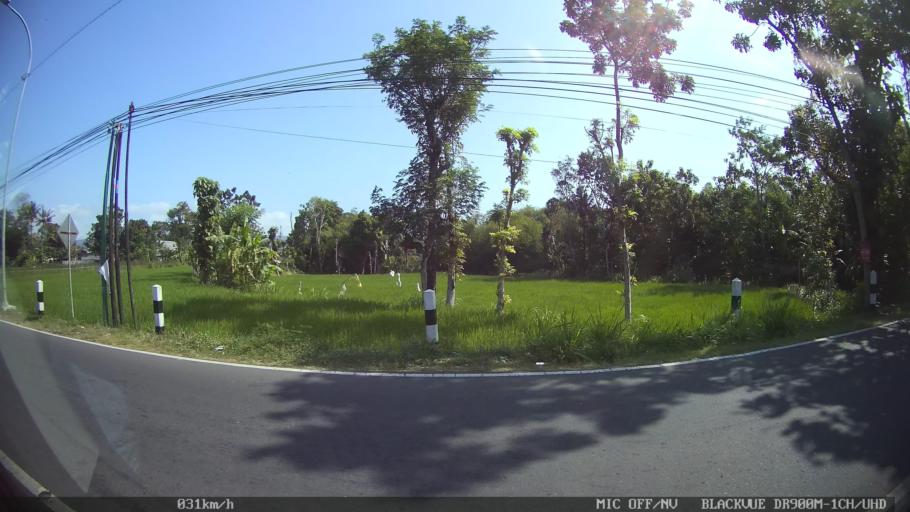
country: ID
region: Daerah Istimewa Yogyakarta
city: Sewon
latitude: -7.9165
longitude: 110.3764
